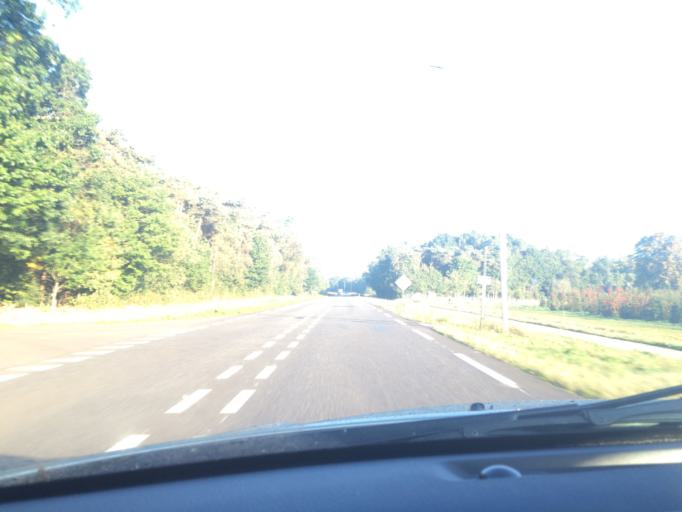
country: NL
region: North Brabant
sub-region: Gemeente Baarle-Nassau
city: Baarle-Nassau
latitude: 51.5213
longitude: 4.9547
